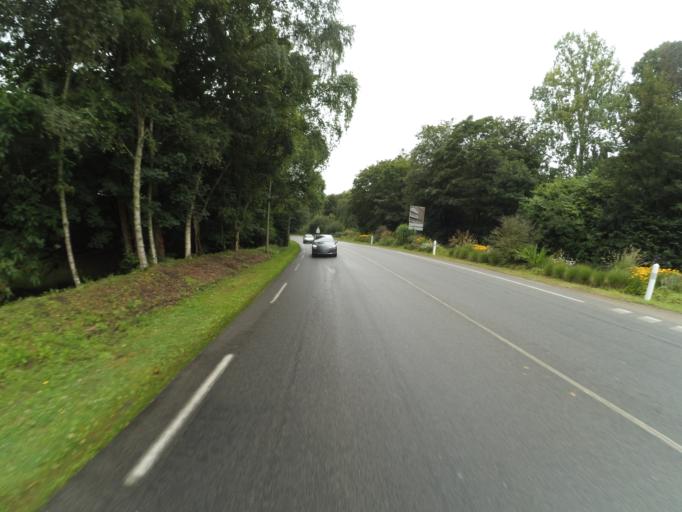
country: FR
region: Brittany
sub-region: Departement du Finistere
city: Morlaix
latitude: 48.5900
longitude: -3.8340
